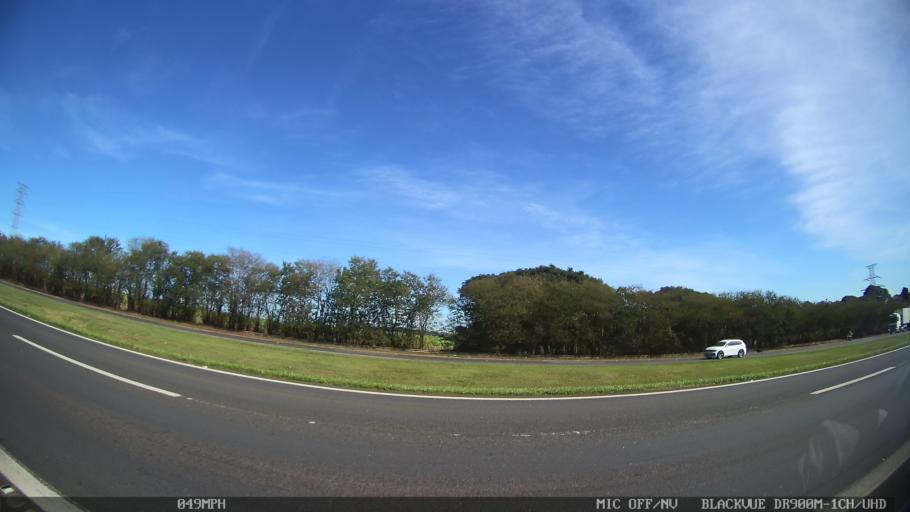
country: BR
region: Sao Paulo
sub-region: Araras
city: Araras
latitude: -22.3162
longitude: -47.3904
